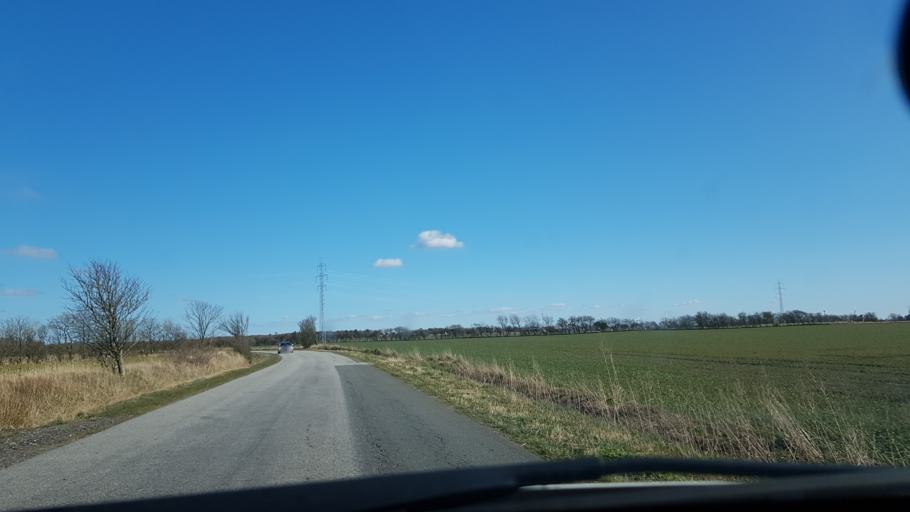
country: DK
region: South Denmark
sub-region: Tonder Kommune
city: Sherrebek
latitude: 55.2222
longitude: 8.8133
